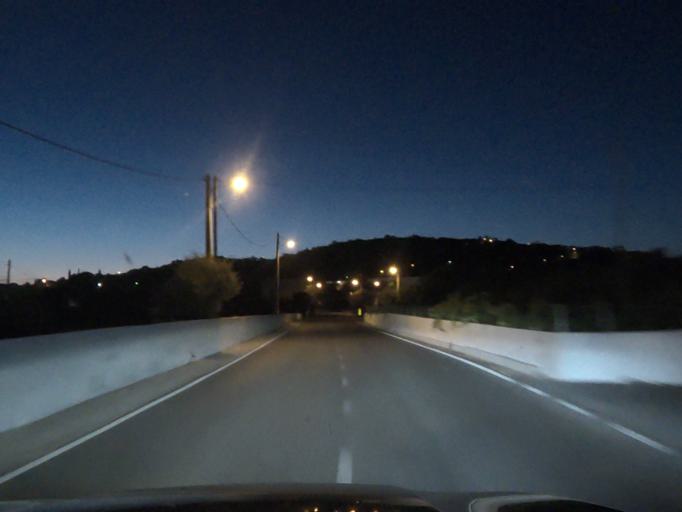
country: PT
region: Faro
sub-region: Loule
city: Loule
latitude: 37.1431
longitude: -8.0099
